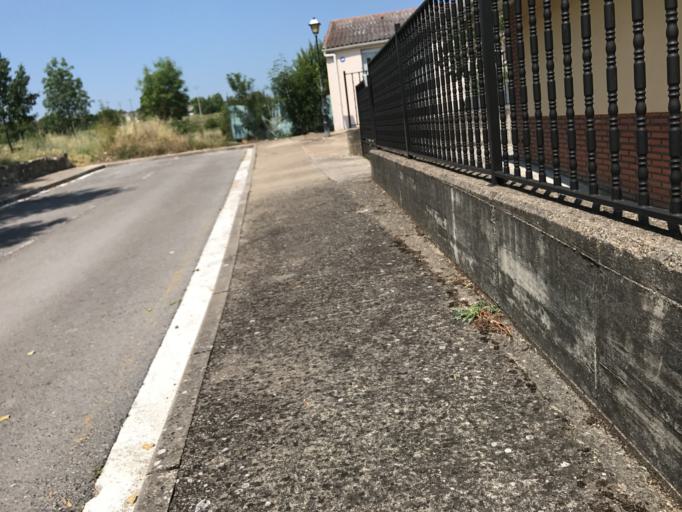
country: ES
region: Basque Country
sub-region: Provincia de Alava
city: Gasteiz / Vitoria
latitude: 42.8795
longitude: -2.6848
